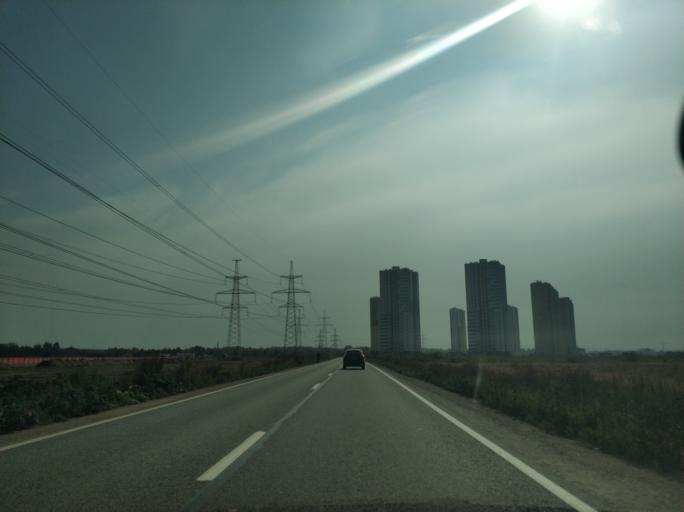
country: RU
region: Leningrad
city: Murino
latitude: 60.0150
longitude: 30.4744
